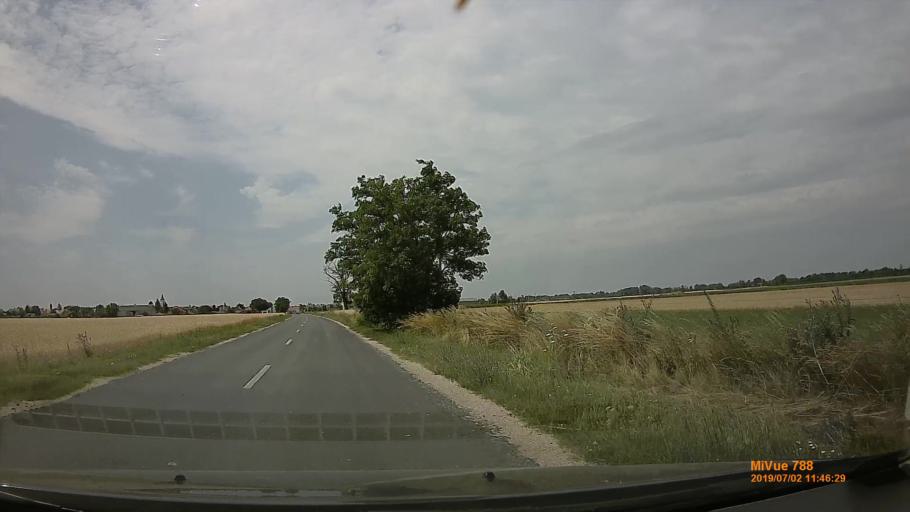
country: HU
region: Gyor-Moson-Sopron
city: Janossomorja
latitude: 47.8599
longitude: 17.1801
